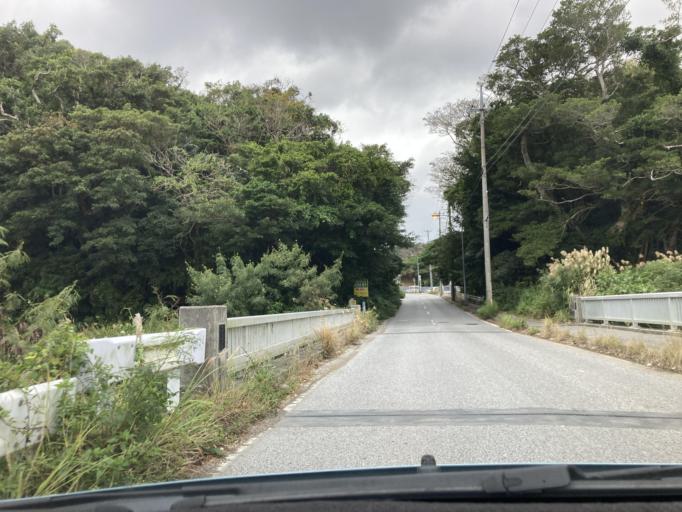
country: JP
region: Okinawa
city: Okinawa
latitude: 26.3465
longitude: 127.8076
